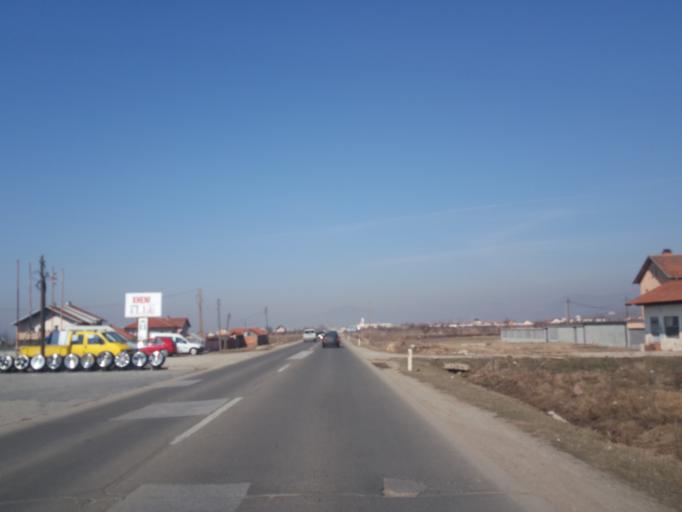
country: XK
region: Mitrovica
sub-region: Vushtrri
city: Vushtrri
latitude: 42.7930
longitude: 21.0023
